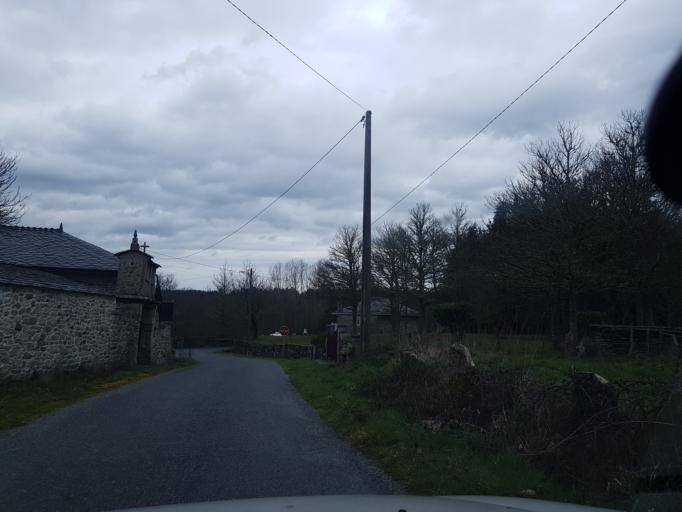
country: ES
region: Galicia
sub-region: Provincia de Lugo
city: Friol
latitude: 43.1211
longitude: -7.8167
